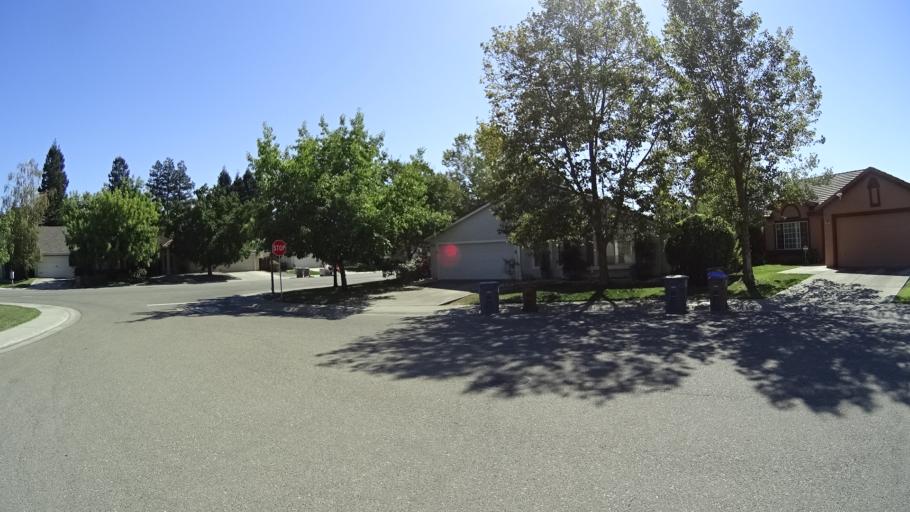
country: US
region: California
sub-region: Sacramento County
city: Laguna
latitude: 38.4262
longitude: -121.4266
